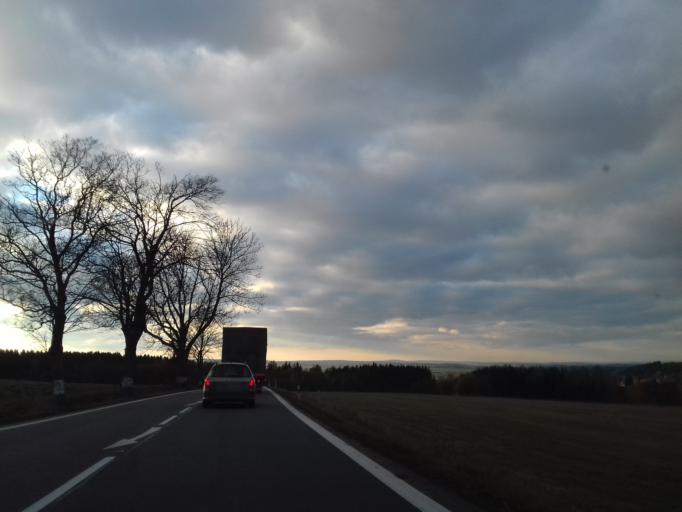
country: CZ
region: Pardubicky
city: Prosec
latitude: 49.7658
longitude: 16.0827
